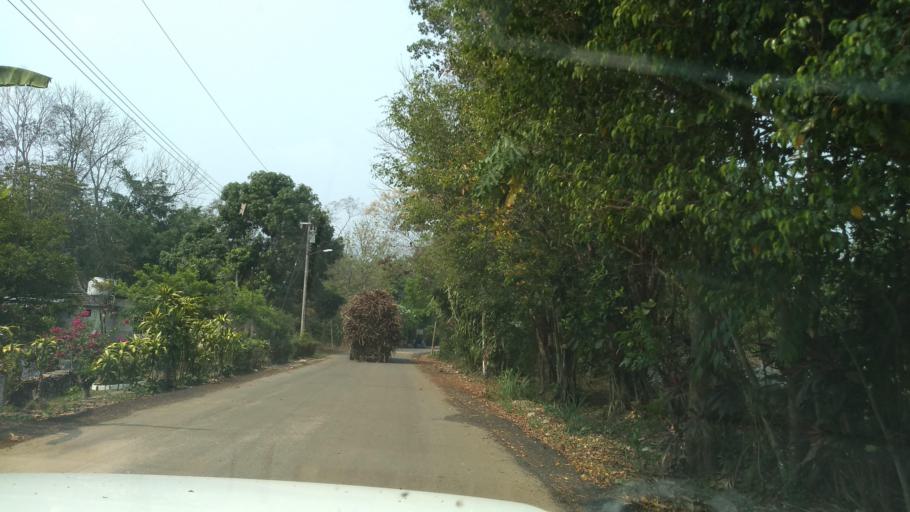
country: MX
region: Veracruz
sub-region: Tezonapa
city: Laguna Chica (Pueblo Nuevo)
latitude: 18.5371
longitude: -96.7848
